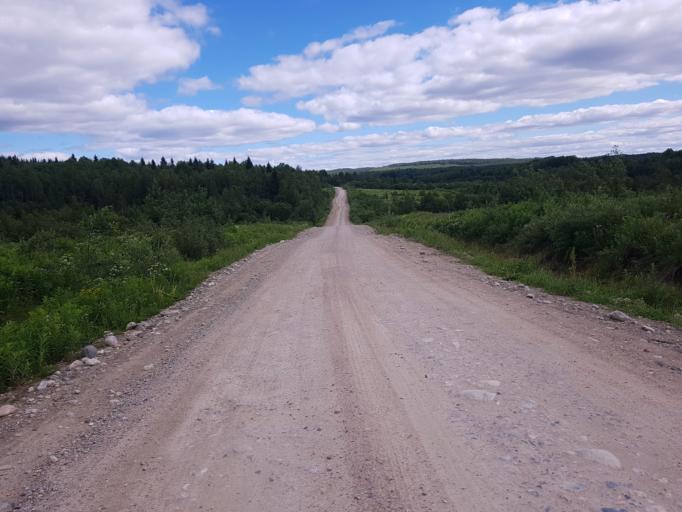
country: RU
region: Republic of Karelia
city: Kostomuksha
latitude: 65.1682
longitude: 30.2969
